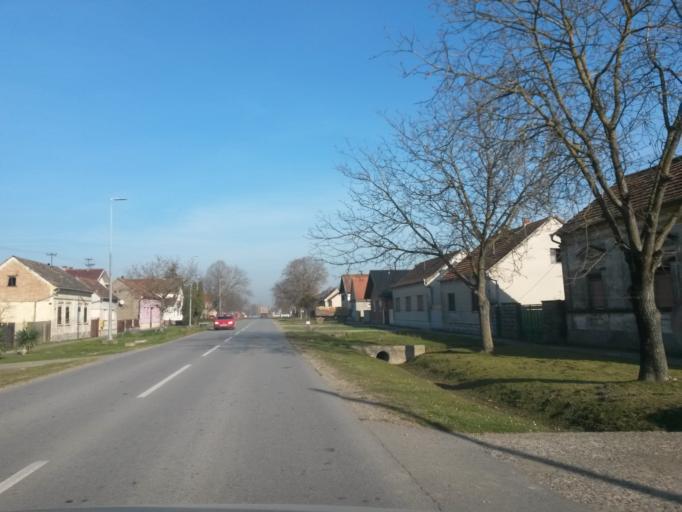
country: HR
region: Vukovarsko-Srijemska
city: Privlaka
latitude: 45.1986
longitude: 18.8430
